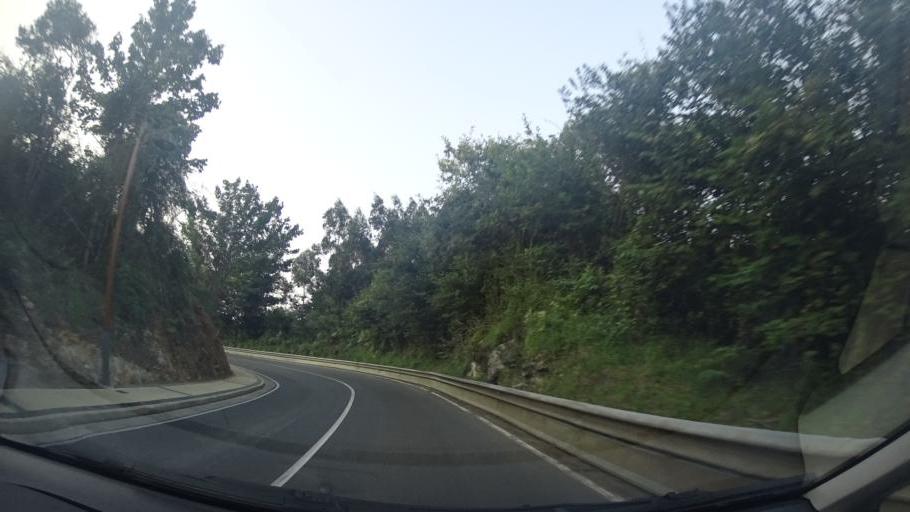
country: ES
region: Asturias
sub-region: Province of Asturias
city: Colunga
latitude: 43.4662
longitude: -5.2004
